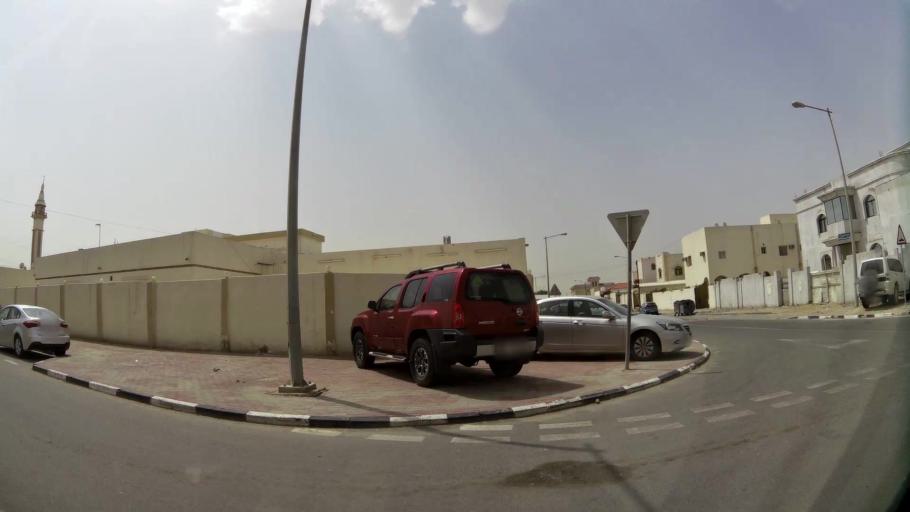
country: QA
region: Baladiyat ar Rayyan
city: Ar Rayyan
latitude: 25.2339
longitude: 51.4299
